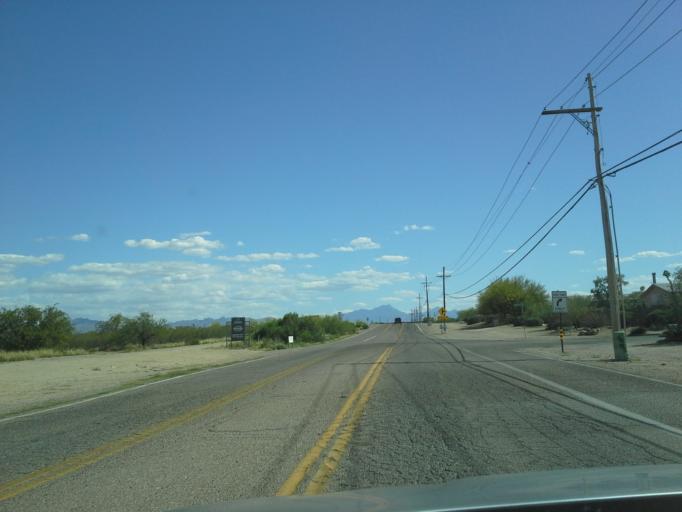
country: US
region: Arizona
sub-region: Pima County
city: Summit
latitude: 32.1223
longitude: -110.8580
